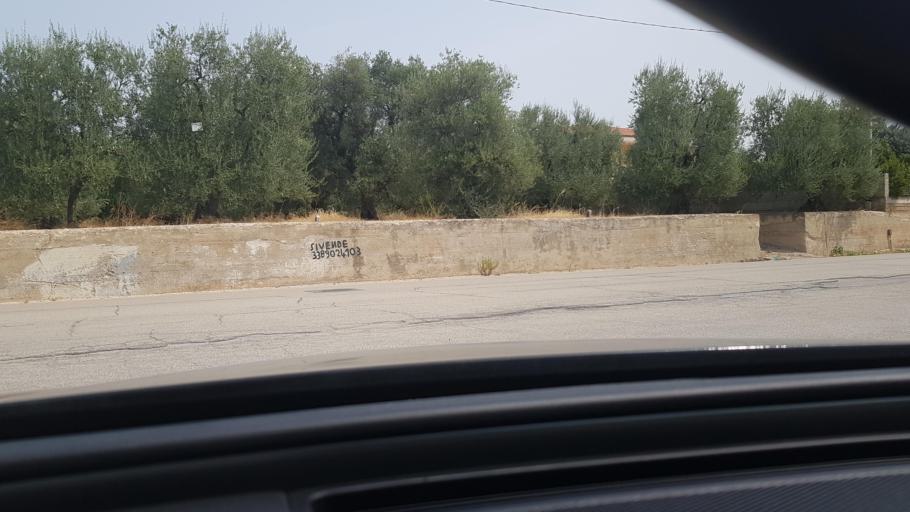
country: IT
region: Apulia
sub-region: Provincia di Barletta - Andria - Trani
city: Andria
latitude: 41.2306
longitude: 16.2752
